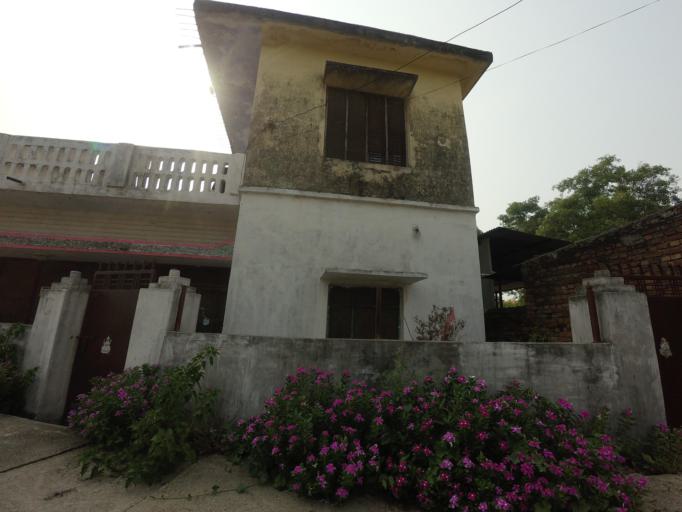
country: NP
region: Western Region
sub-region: Lumbini Zone
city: Bhairahawa
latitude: 27.5198
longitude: 83.4555
